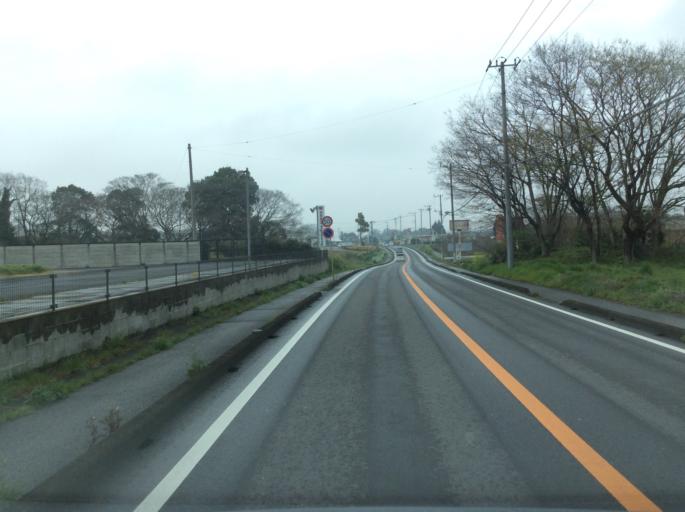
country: JP
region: Ibaraki
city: Mitsukaido
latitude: 35.9881
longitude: 139.9363
